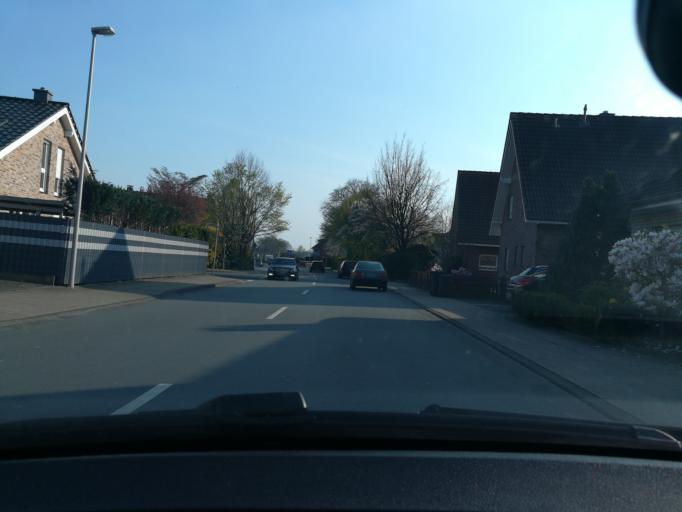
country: DE
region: North Rhine-Westphalia
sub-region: Regierungsbezirk Detmold
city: Bielefeld
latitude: 51.9976
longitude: 8.4741
